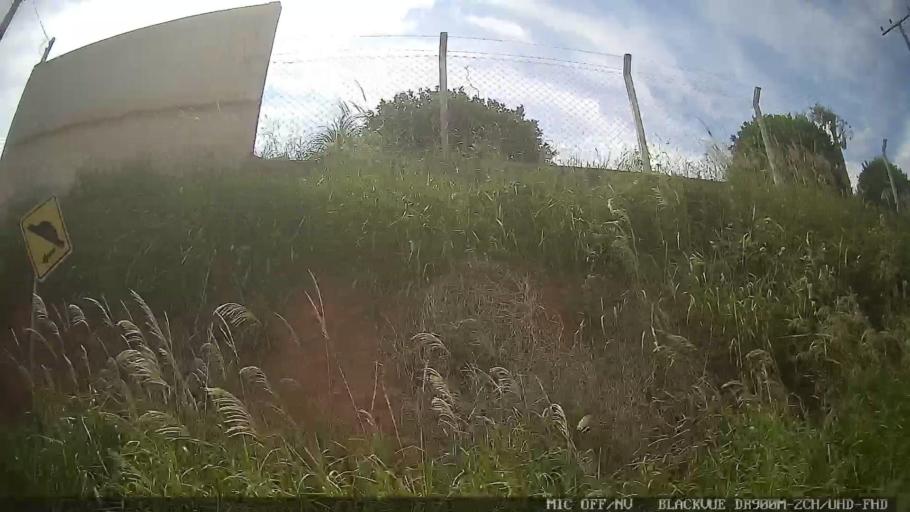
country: BR
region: Sao Paulo
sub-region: Braganca Paulista
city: Braganca Paulista
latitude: -22.9852
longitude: -46.6461
